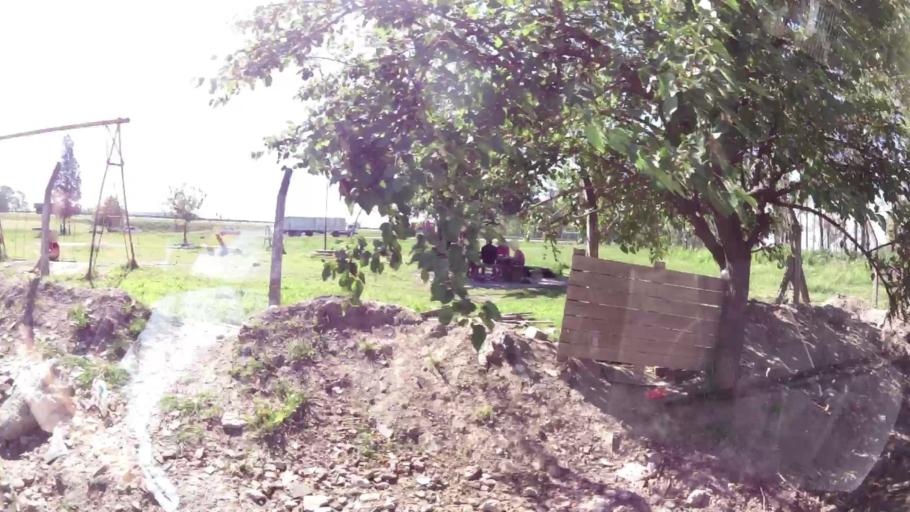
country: AR
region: Buenos Aires
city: Hurlingham
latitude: -34.5321
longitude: -58.5942
